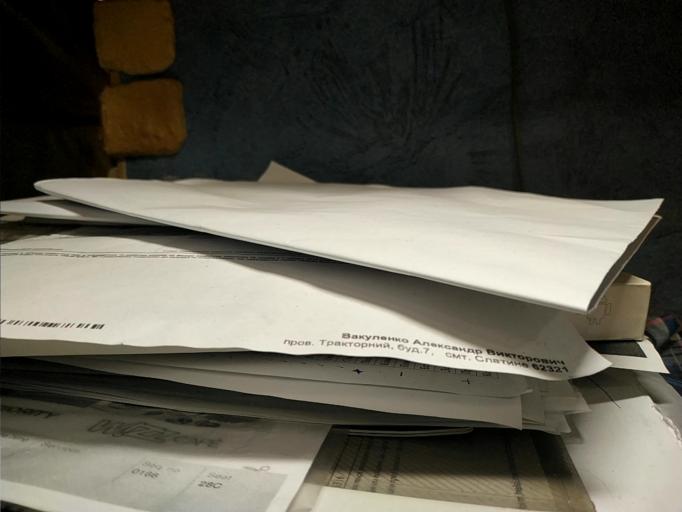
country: RU
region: Tverskaya
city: Zubtsov
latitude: 56.0996
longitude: 34.6910
